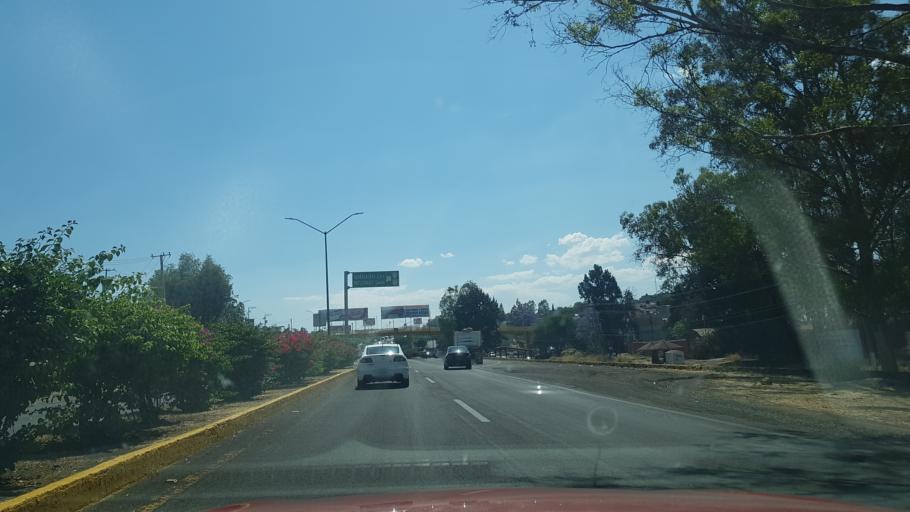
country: MX
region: Michoacan
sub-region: Morelia
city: La Aldea
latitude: 19.7174
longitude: -101.1532
